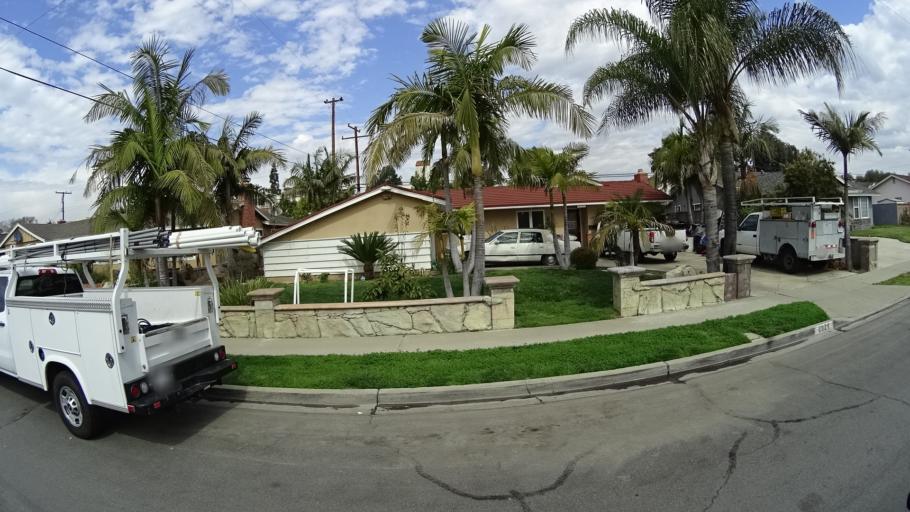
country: US
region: California
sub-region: Orange County
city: Anaheim
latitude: 33.8360
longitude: -117.8839
